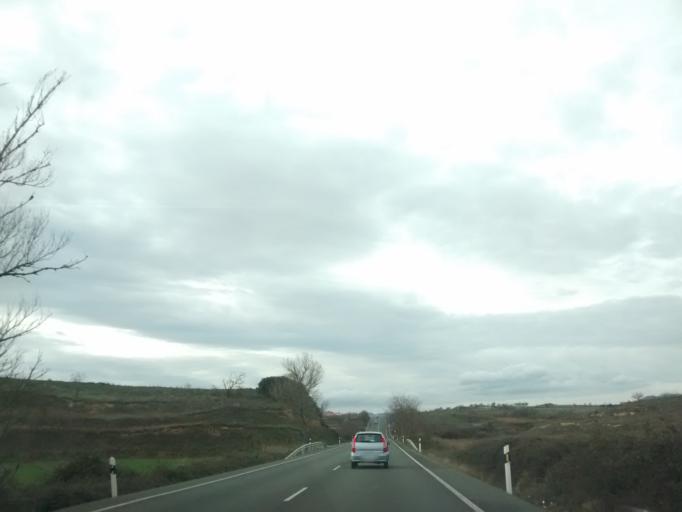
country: ES
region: La Rioja
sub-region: Provincia de La Rioja
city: Briones
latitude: 42.5290
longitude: -2.7600
